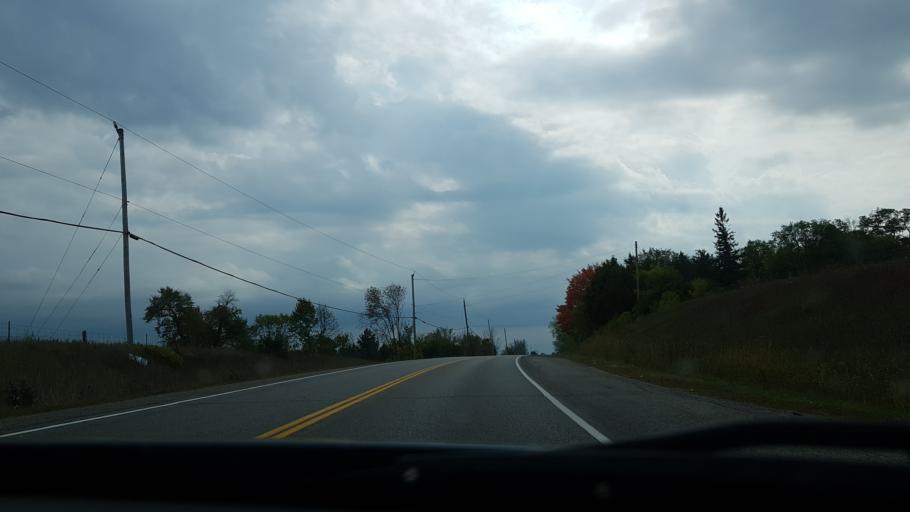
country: CA
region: Ontario
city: Omemee
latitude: 44.5029
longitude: -78.7419
